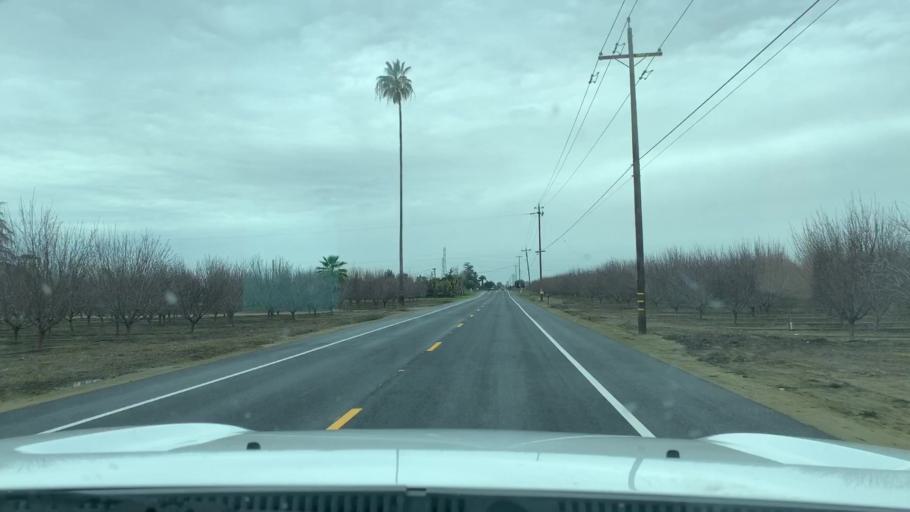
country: US
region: California
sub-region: Fresno County
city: Fowler
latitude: 36.5879
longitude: -119.6825
